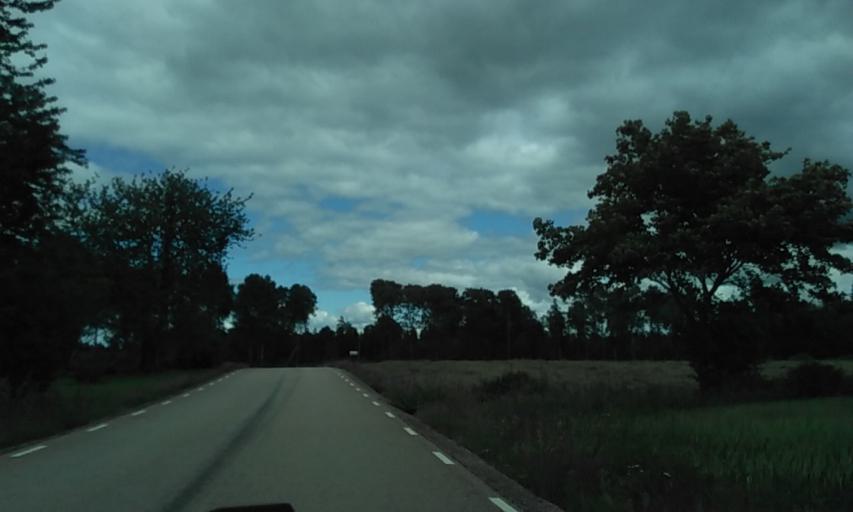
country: SE
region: Vaestra Goetaland
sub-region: Boras Kommun
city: Sjomarken
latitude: 57.7947
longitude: 12.8762
